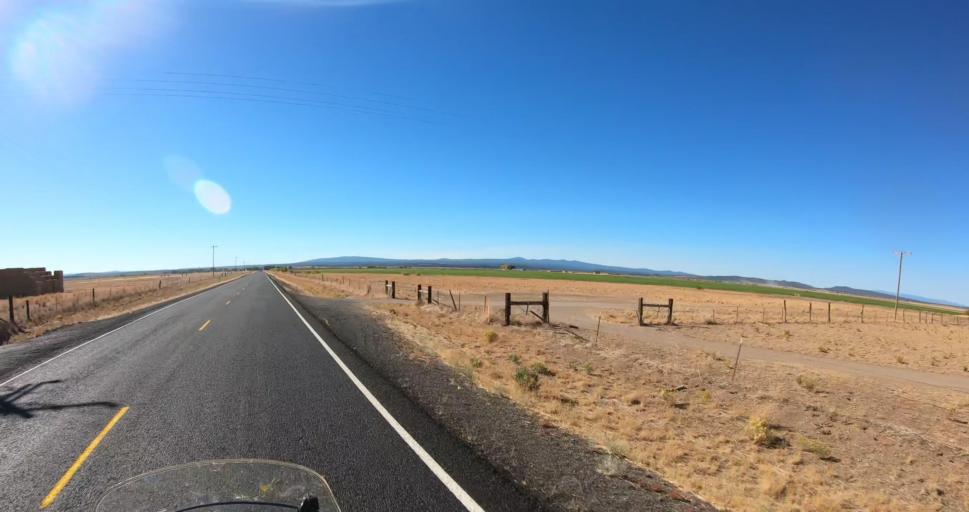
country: US
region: Oregon
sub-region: Deschutes County
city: La Pine
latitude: 43.1277
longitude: -121.0163
